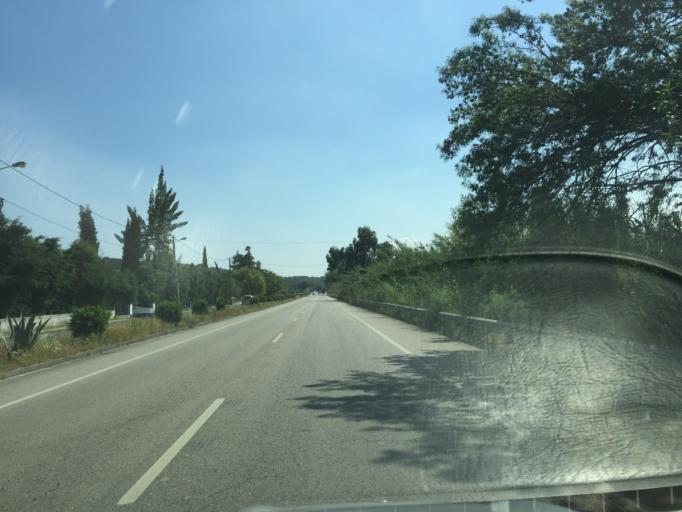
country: PT
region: Santarem
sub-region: Golega
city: Golega
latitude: 39.3970
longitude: -8.4371
